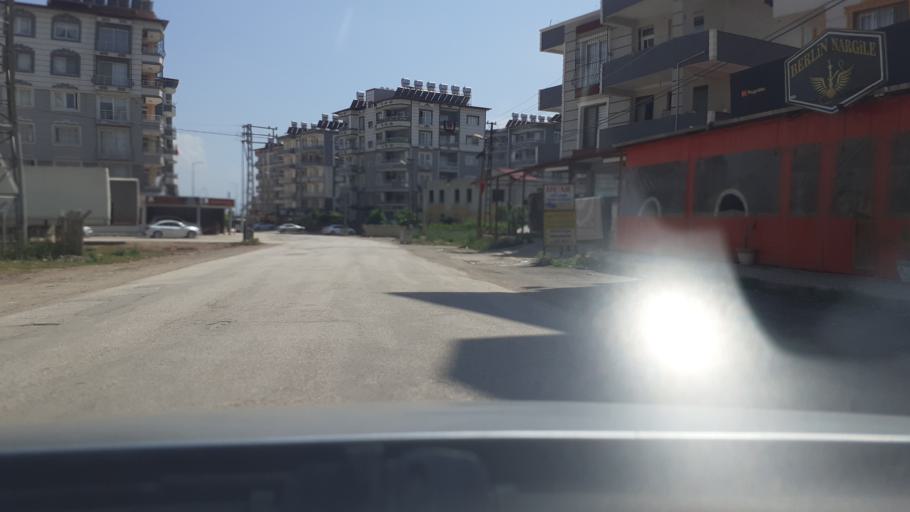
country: TR
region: Hatay
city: Kirikhan
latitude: 36.4821
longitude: 36.3554
